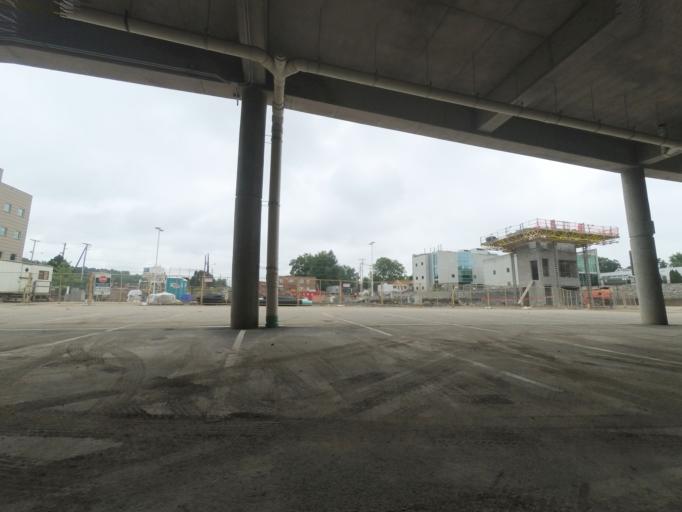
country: US
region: West Virginia
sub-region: Cabell County
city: Huntington
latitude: 38.4112
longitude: -82.4303
